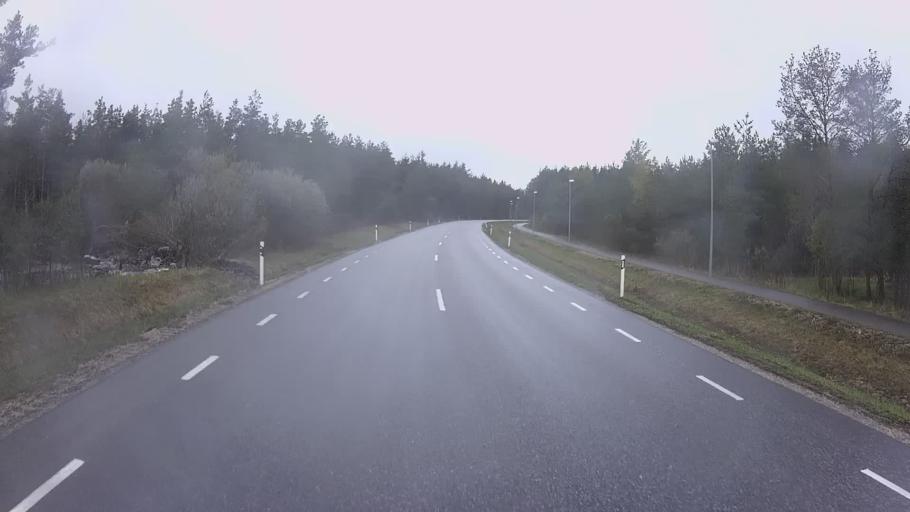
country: EE
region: Hiiumaa
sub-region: Kaerdla linn
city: Kardla
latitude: 58.9806
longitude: 22.5095
